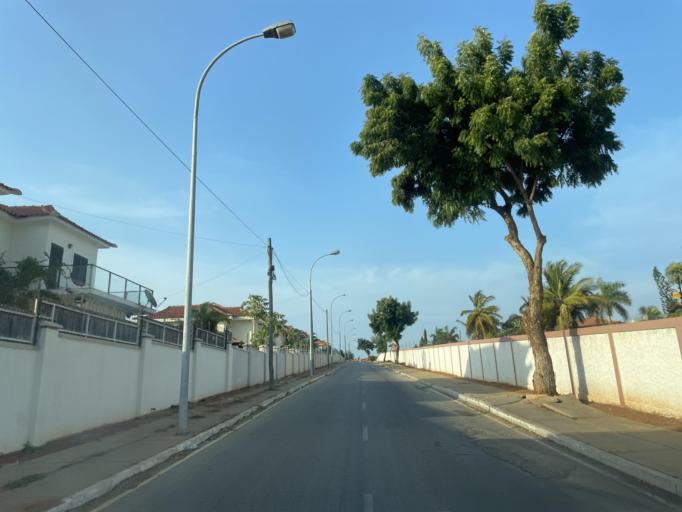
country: AO
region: Luanda
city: Luanda
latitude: -8.9298
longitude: 13.1798
